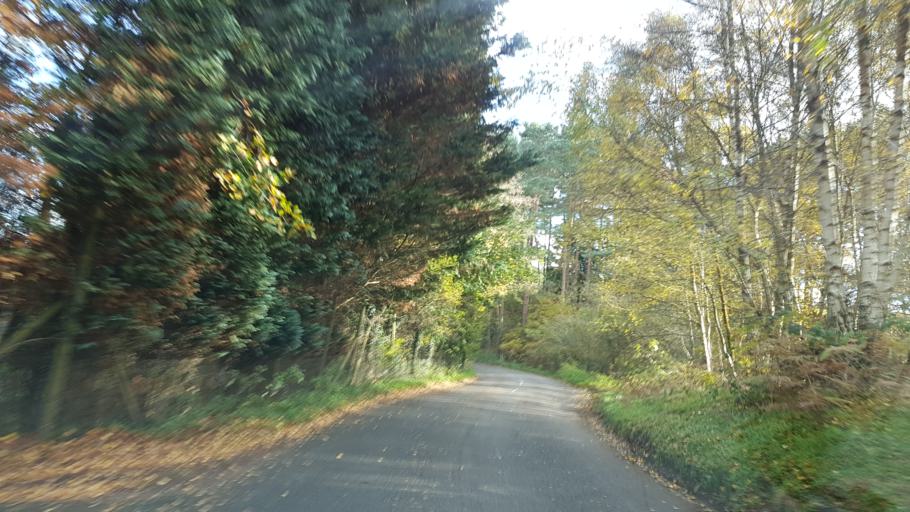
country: GB
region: England
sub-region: Surrey
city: Seale
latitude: 51.2223
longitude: -0.7074
